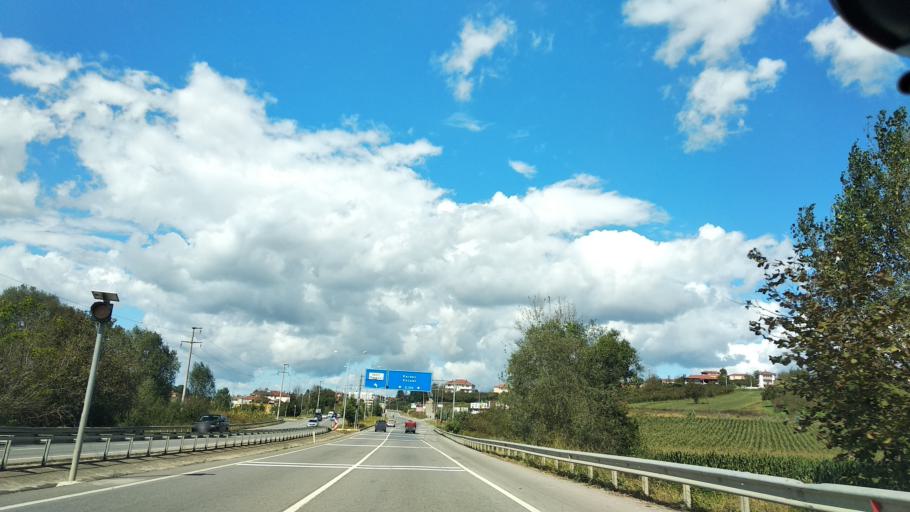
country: TR
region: Sakarya
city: Ferizli
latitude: 40.9266
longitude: 30.4900
